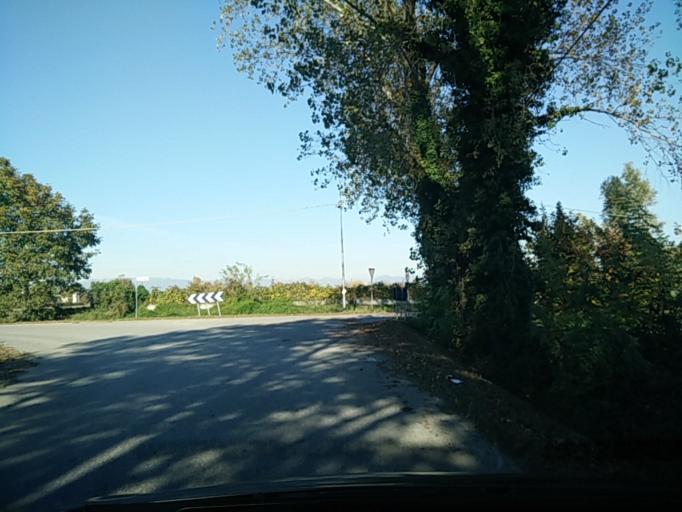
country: IT
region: Veneto
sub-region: Provincia di Treviso
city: Varago
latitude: 45.7212
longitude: 12.2975
